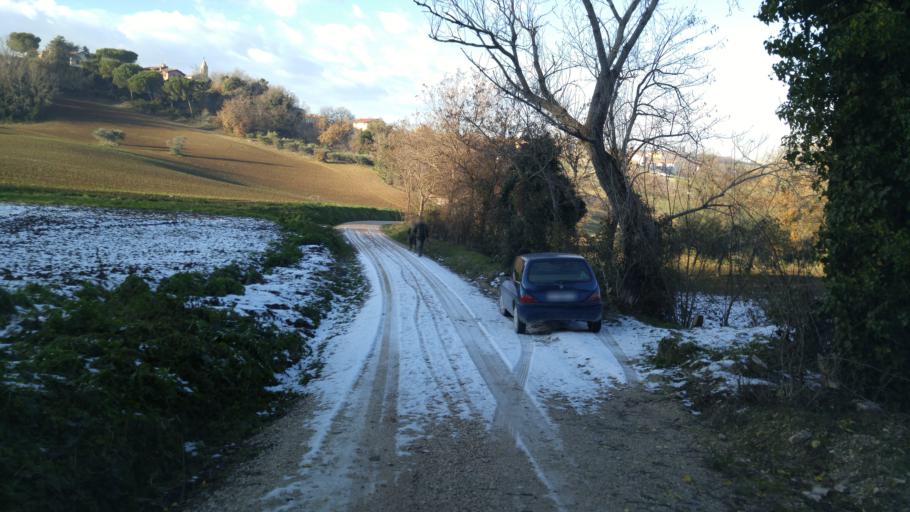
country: IT
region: The Marches
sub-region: Provincia di Pesaro e Urbino
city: Piagge
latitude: 43.7300
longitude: 12.9711
